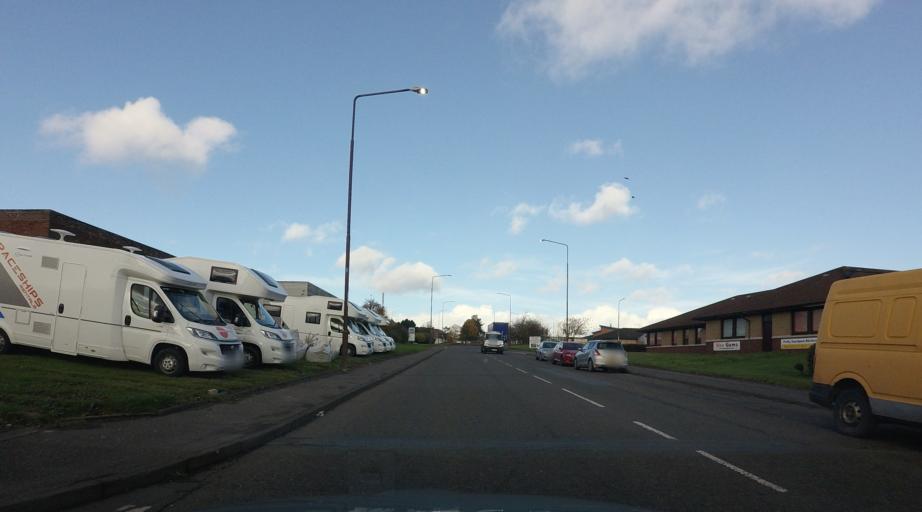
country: GB
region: Scotland
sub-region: West Lothian
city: Broxburn
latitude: 55.9365
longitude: -3.4527
